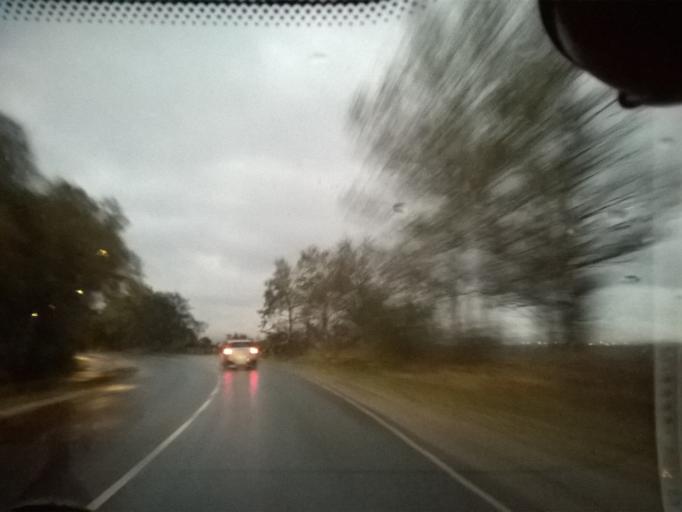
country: EE
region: Harju
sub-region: Viimsi vald
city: Rummu
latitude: 59.5341
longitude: 24.7932
